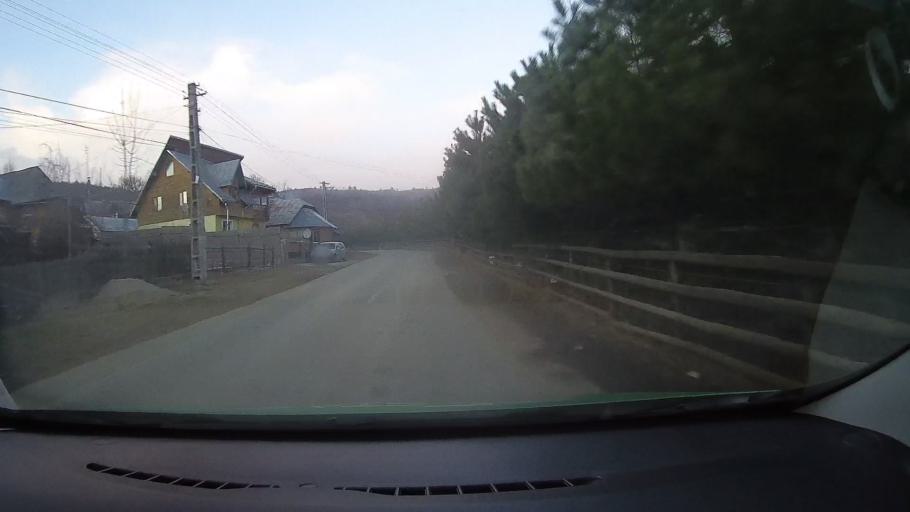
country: RO
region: Prahova
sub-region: Comuna Secaria
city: Secaria
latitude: 45.2751
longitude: 25.6868
